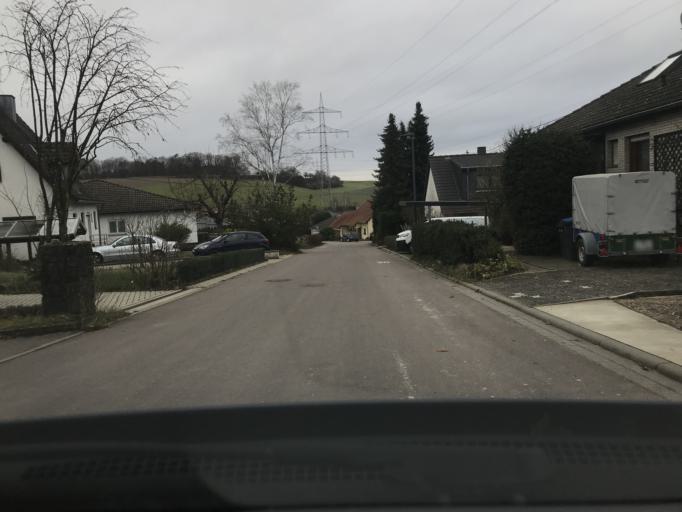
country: DE
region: Rheinland-Pfalz
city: Newel
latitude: 49.7895
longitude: 6.5700
